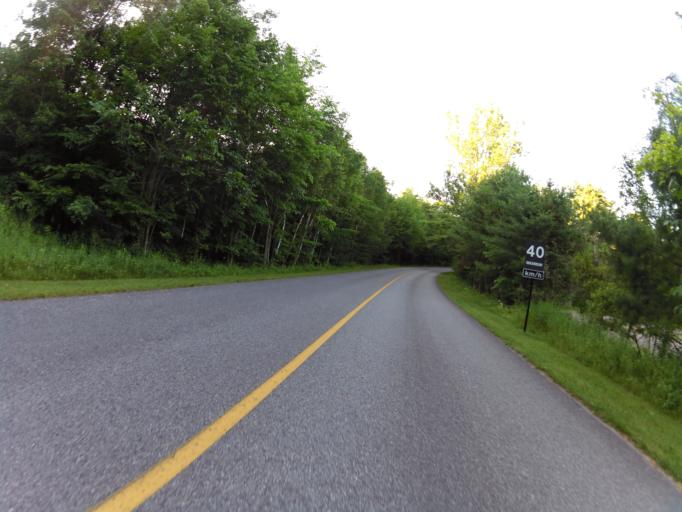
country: CA
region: Quebec
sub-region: Outaouais
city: Wakefield
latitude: 45.6145
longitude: -76.0109
